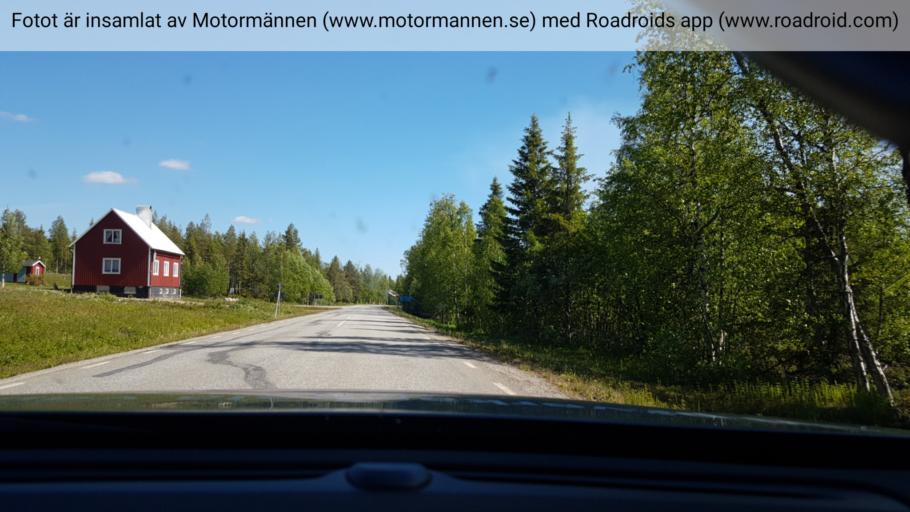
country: SE
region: Vaesterbotten
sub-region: Lycksele Kommun
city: Soderfors
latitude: 64.6817
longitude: 17.8154
